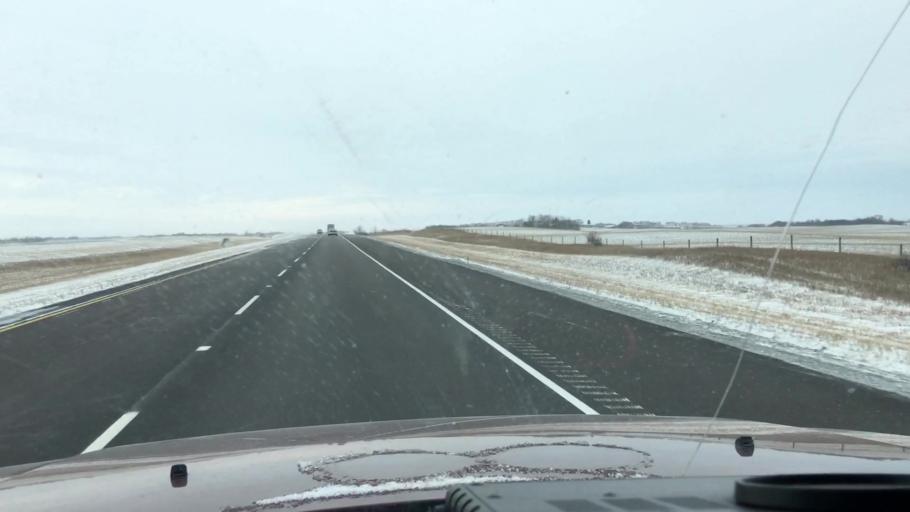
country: CA
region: Saskatchewan
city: Saskatoon
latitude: 51.6985
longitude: -106.4608
